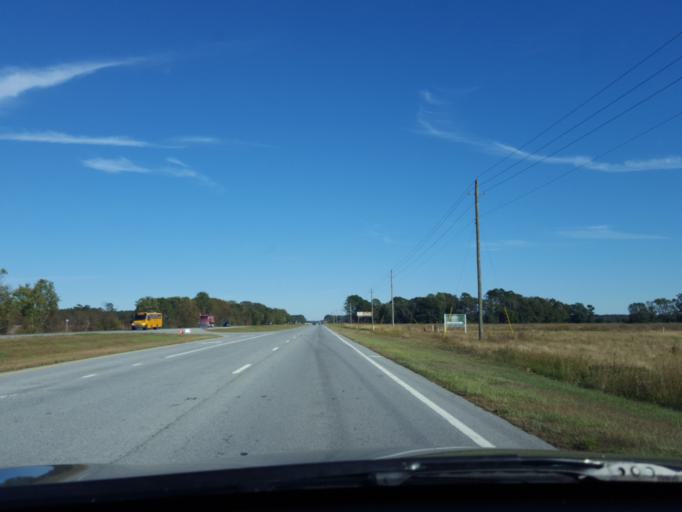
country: US
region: North Carolina
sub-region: Pitt County
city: Greenville
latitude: 35.6257
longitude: -77.3074
